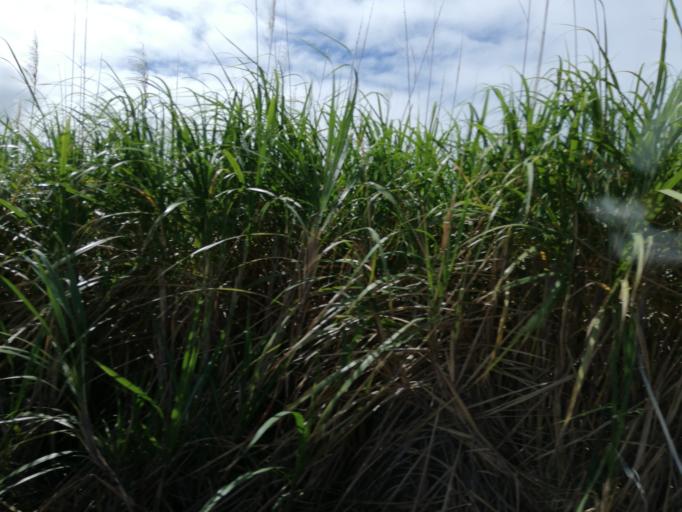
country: MU
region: Grand Port
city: Plaine Magnien
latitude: -20.4615
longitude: 57.6572
